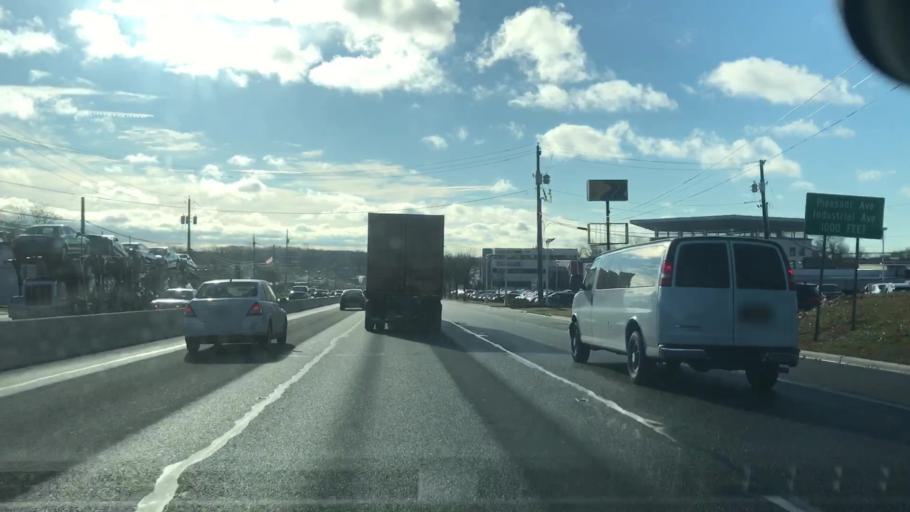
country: US
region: New Jersey
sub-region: Bergen County
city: Allendale
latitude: 41.0541
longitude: -74.1199
